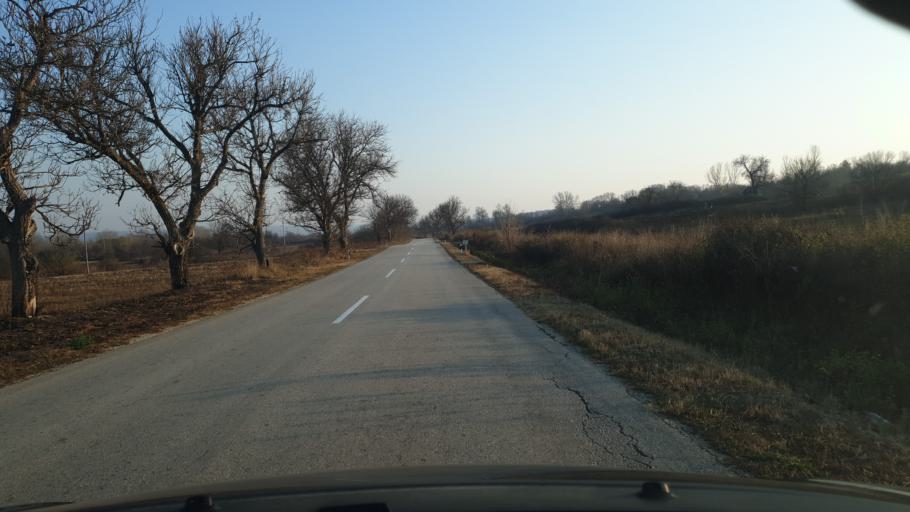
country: RS
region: Central Serbia
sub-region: Zajecarski Okrug
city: Zajecar
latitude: 43.9858
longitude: 22.2864
